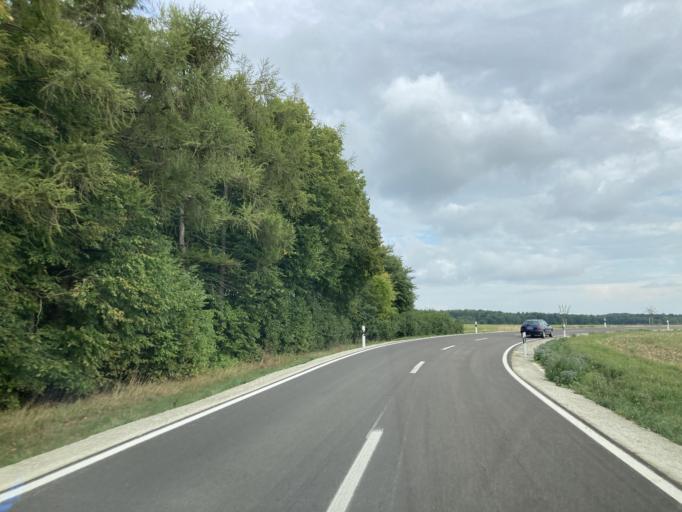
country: DE
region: Bavaria
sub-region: Swabia
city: Forheim
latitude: 48.7937
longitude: 10.4174
